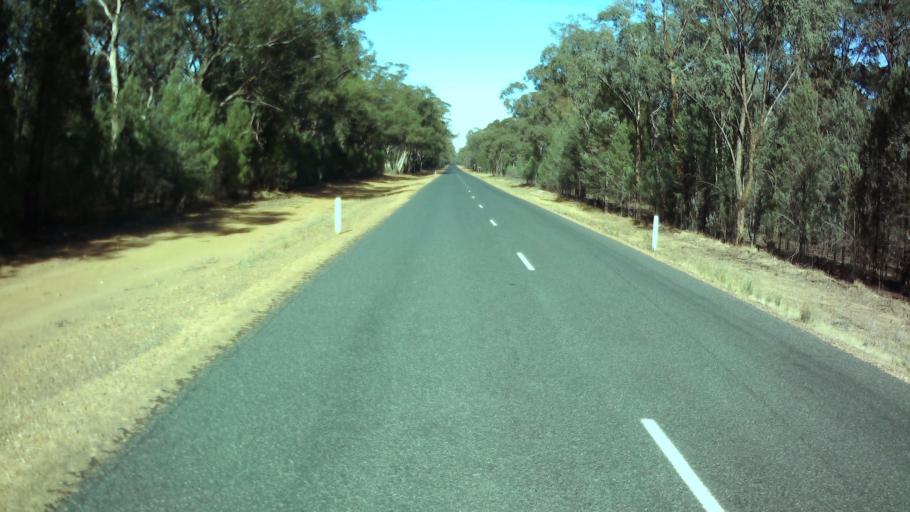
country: AU
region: New South Wales
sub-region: Weddin
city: Grenfell
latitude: -34.0243
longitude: 148.0183
